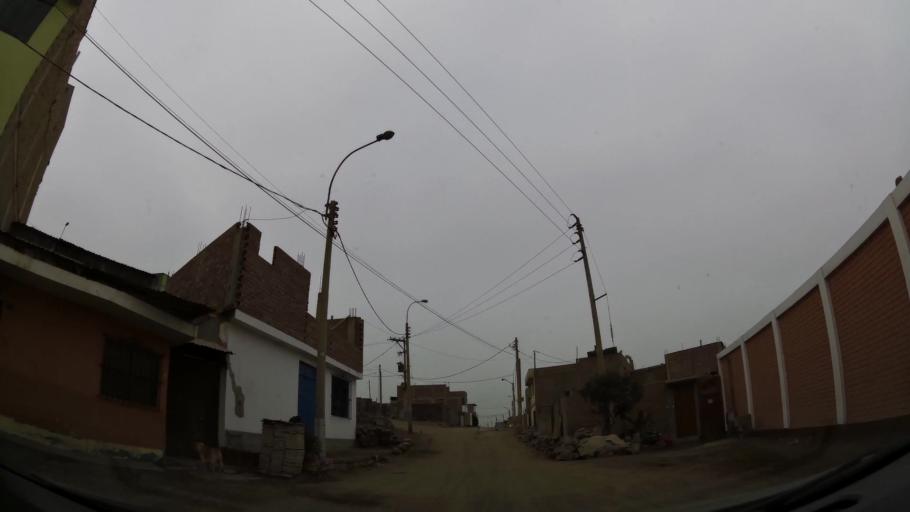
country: PE
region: Lima
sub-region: Lima
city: Surco
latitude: -12.2052
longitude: -76.9902
